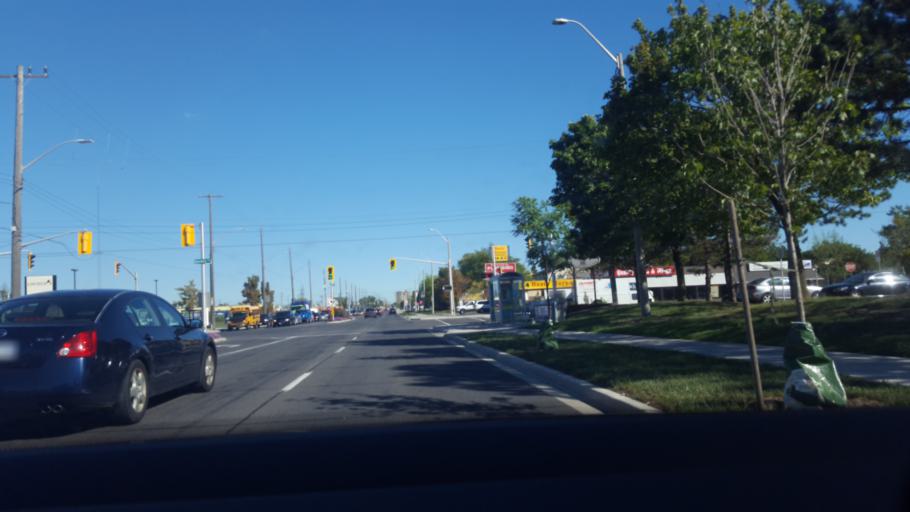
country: CA
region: Ontario
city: Hamilton
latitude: 43.2382
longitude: -79.7661
